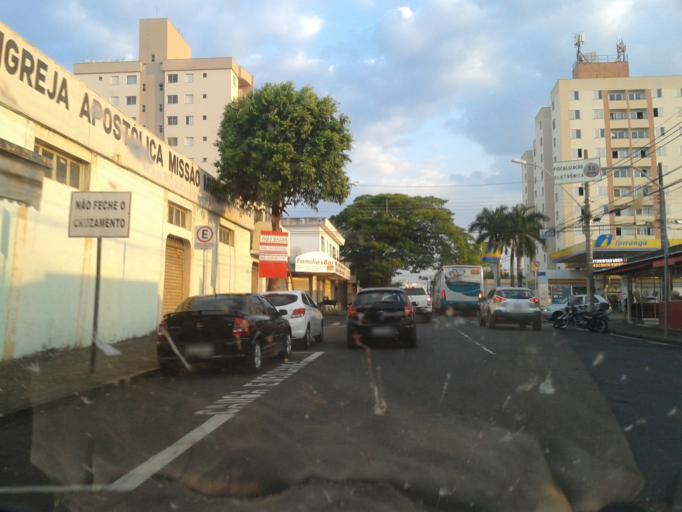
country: BR
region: Minas Gerais
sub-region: Uberlandia
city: Uberlandia
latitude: -18.9064
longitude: -48.2786
